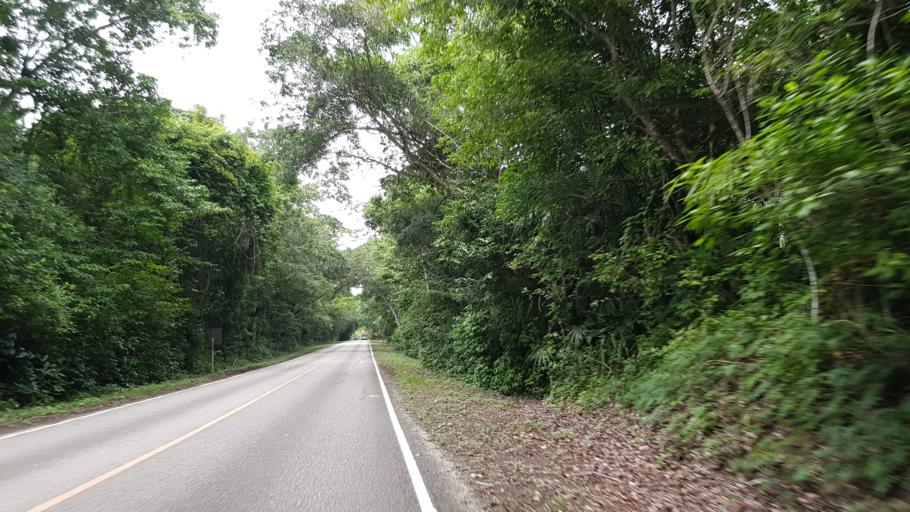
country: GT
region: Peten
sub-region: Municipio de San Jose
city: San Jose
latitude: 17.2201
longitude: -89.6117
